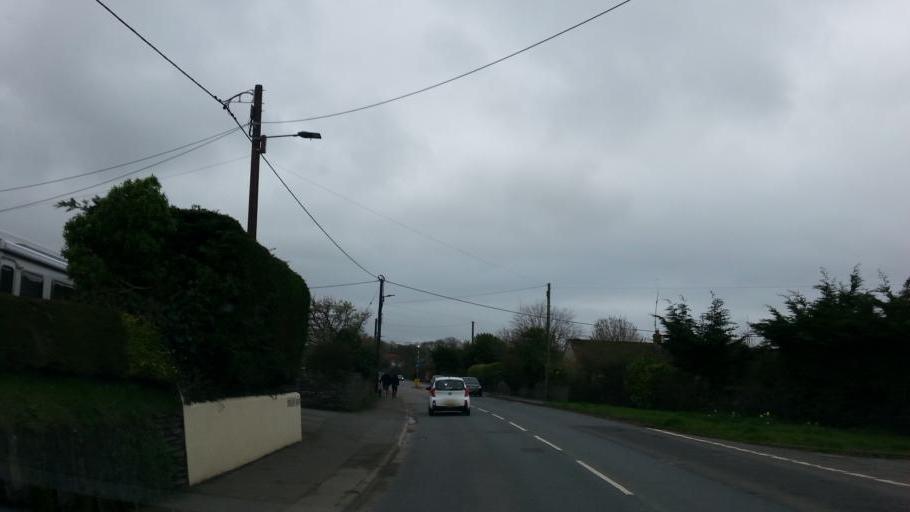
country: GB
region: England
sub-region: Devon
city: Fremington
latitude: 51.0722
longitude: -4.1276
